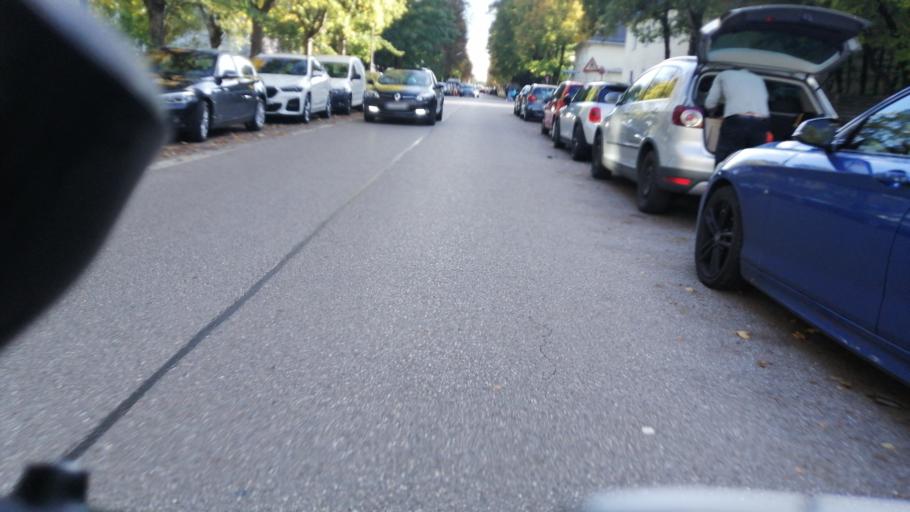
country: DE
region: Bavaria
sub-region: Upper Bavaria
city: Unterfoehring
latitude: 48.1946
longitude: 11.6135
